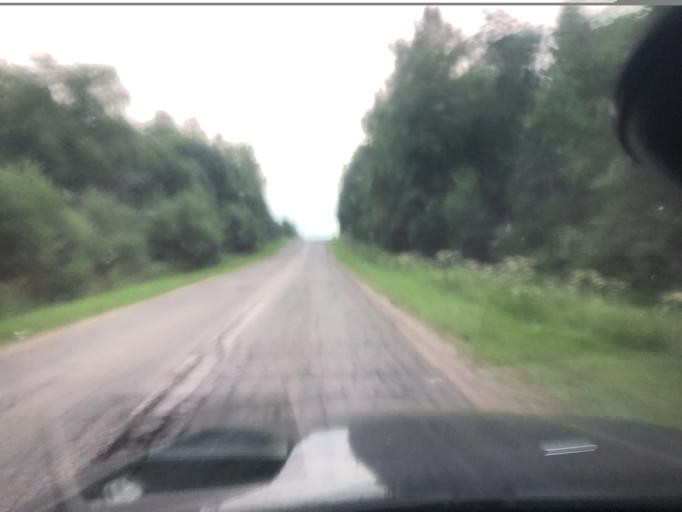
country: RU
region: Jaroslavl
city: Petrovsk
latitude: 56.9975
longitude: 39.1003
